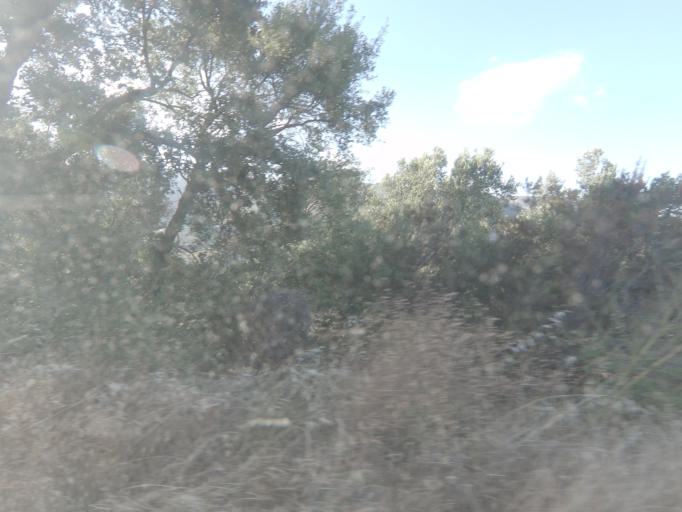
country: PT
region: Viseu
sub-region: Tabuaco
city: Tabuaco
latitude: 41.1517
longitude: -7.5893
